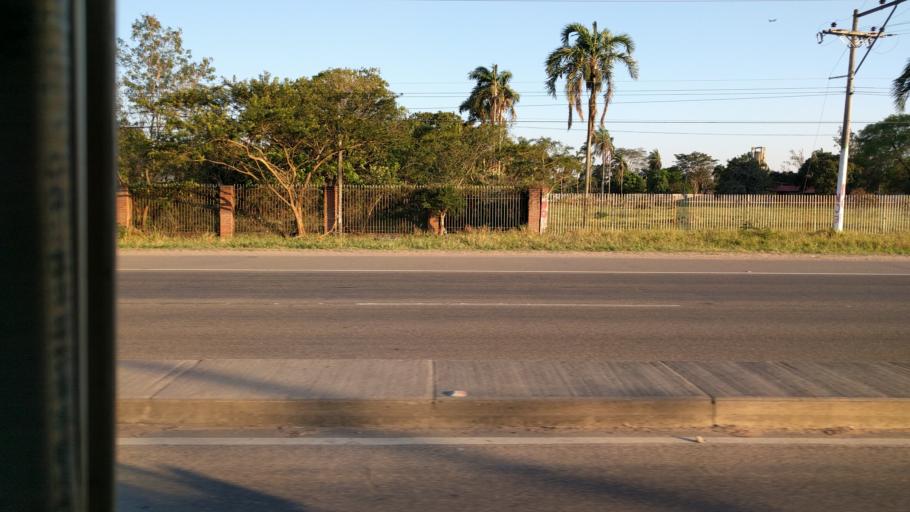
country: BO
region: Santa Cruz
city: Cotoca
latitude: -17.7641
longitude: -63.0330
